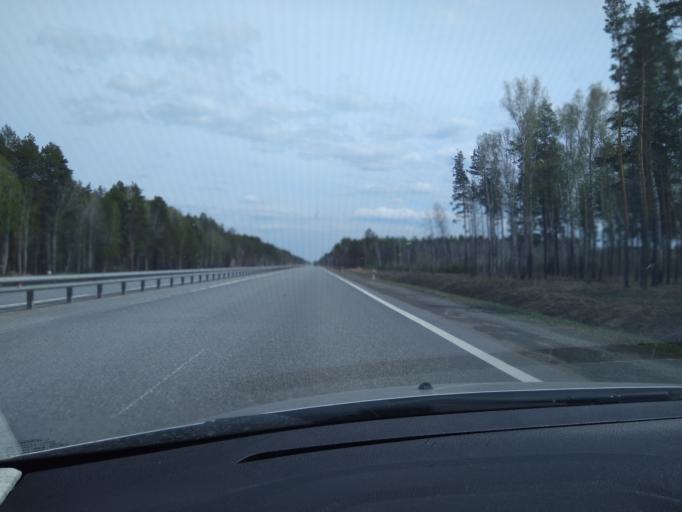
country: RU
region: Sverdlovsk
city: Yushala
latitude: 57.0959
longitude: 64.3782
